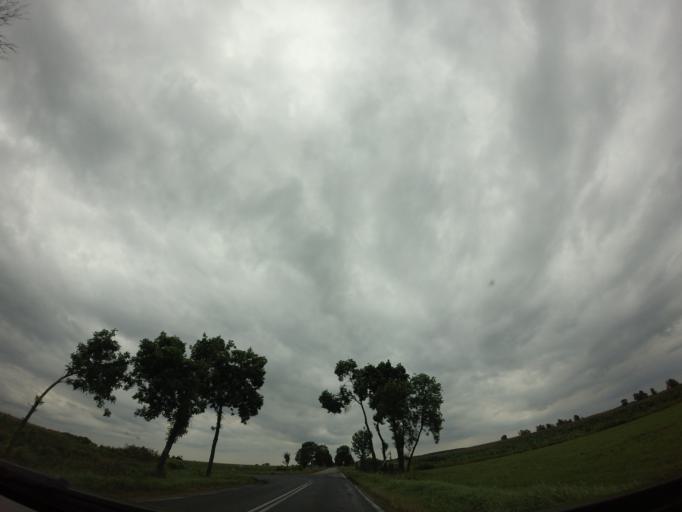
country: PL
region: Masovian Voivodeship
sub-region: Powiat makowski
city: Sypniewo
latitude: 52.9845
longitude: 21.2772
